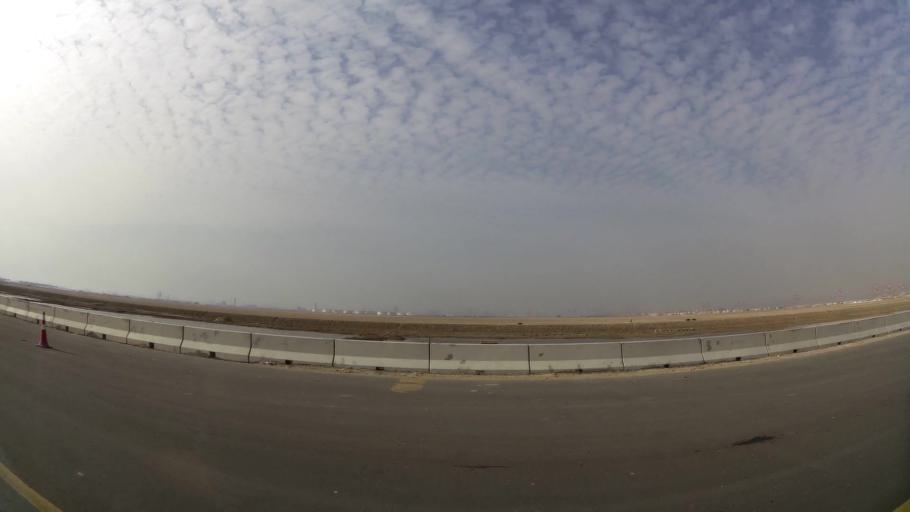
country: AE
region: Abu Dhabi
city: Abu Dhabi
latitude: 24.2804
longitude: 54.5296
